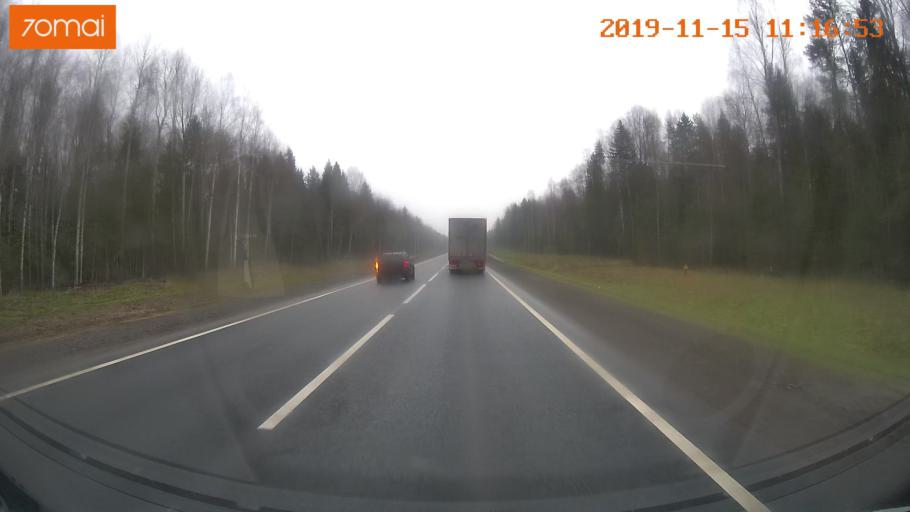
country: RU
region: Vologda
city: Chebsara
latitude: 59.1315
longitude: 39.2393
